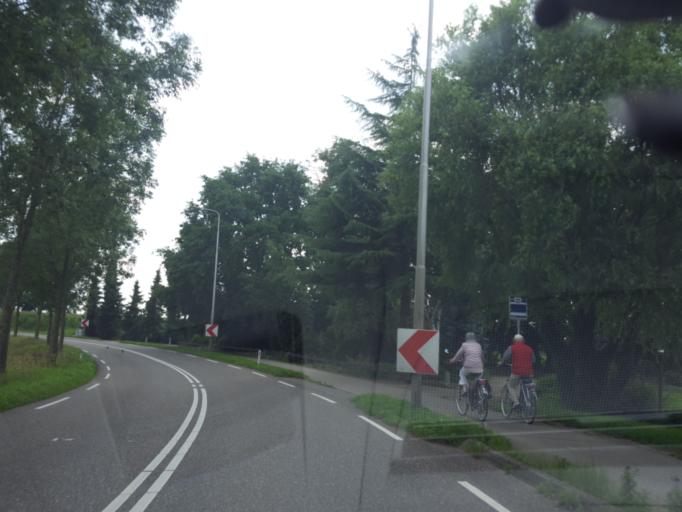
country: NL
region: Limburg
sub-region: Gemeente Bergen
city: Wellerlooi
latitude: 51.5195
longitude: 6.0812
